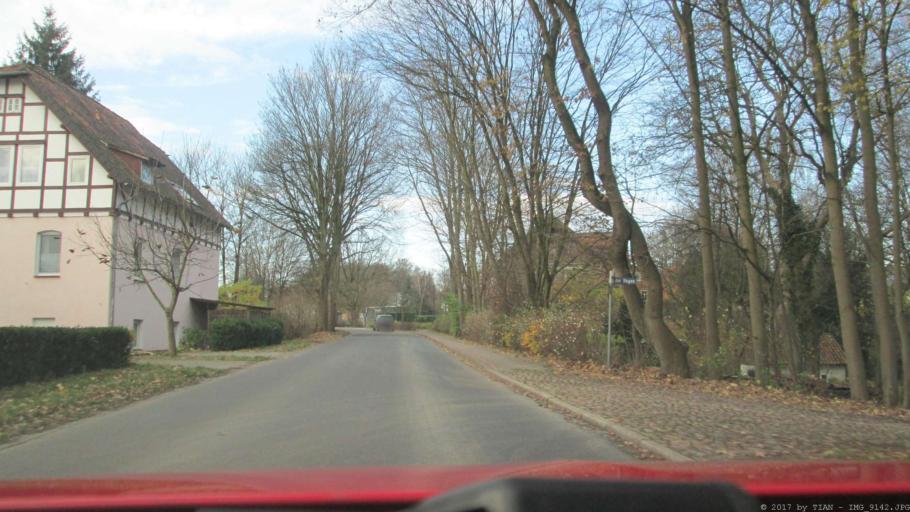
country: DE
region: Lower Saxony
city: Hankensbuttel
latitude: 52.7259
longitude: 10.6111
